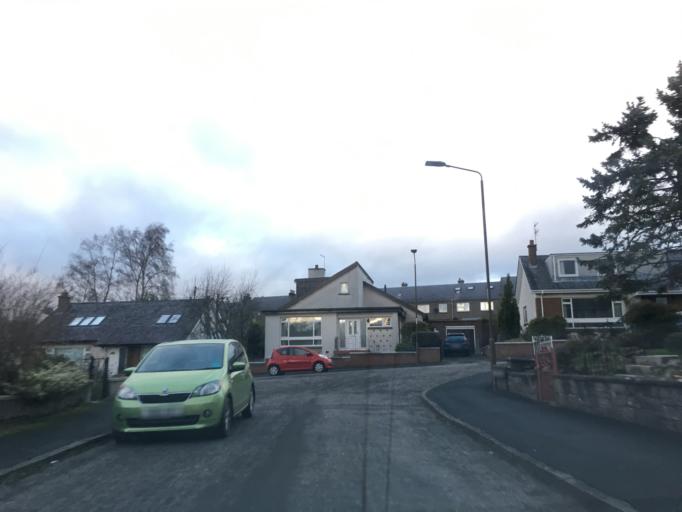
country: GB
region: Scotland
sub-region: Stirling
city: Stirling
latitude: 56.1091
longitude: -3.9431
